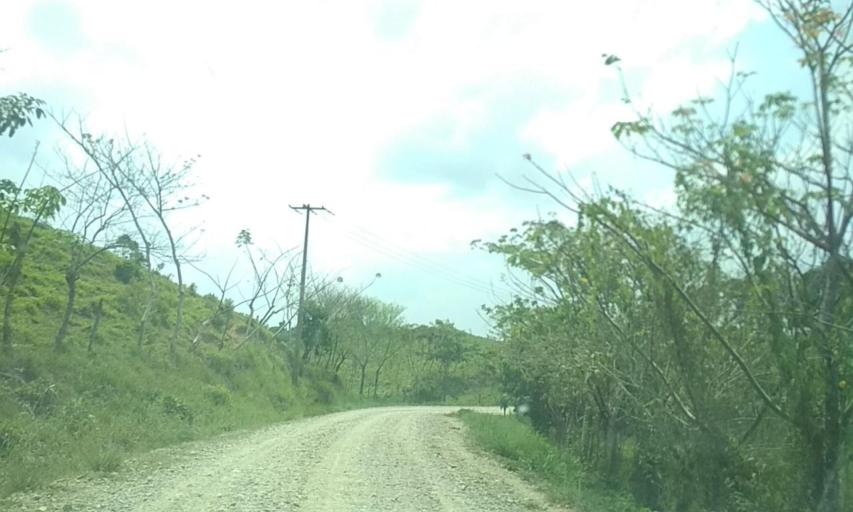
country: MX
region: Tabasco
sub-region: Huimanguillo
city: Francisco Rueda
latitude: 17.6246
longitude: -93.8169
